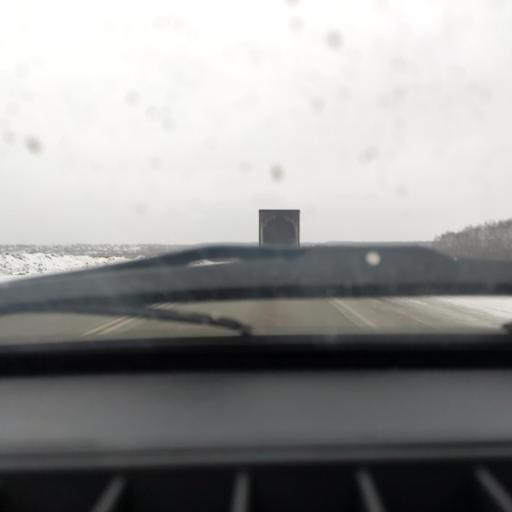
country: RU
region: Bashkortostan
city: Iglino
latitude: 54.7300
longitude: 56.2590
